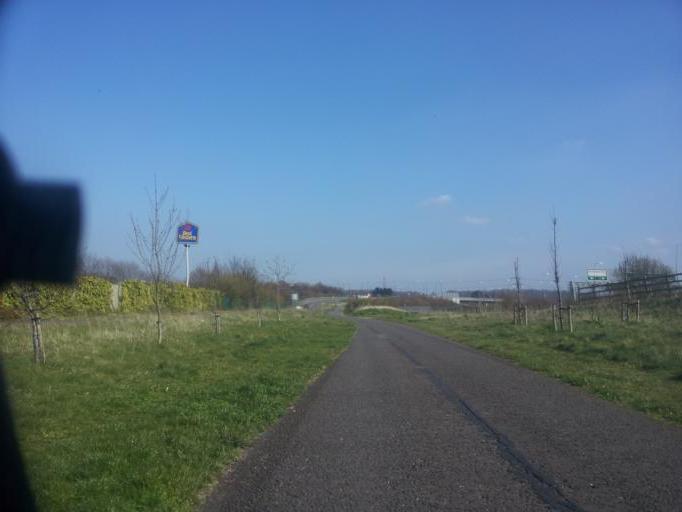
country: GB
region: England
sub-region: Kent
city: Gravesend
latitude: 51.4103
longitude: 0.3790
